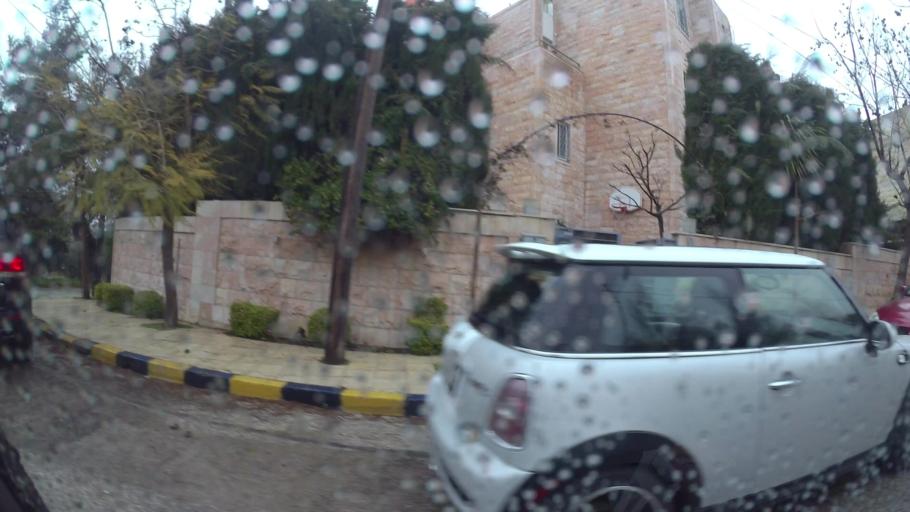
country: JO
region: Amman
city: Al Jubayhah
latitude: 31.9983
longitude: 35.8278
